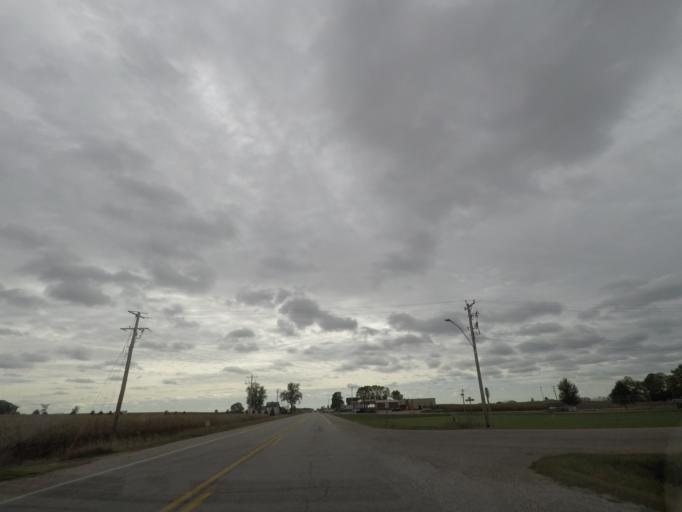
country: US
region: Iowa
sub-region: Story County
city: Nevada
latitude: 42.0167
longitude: -93.3095
